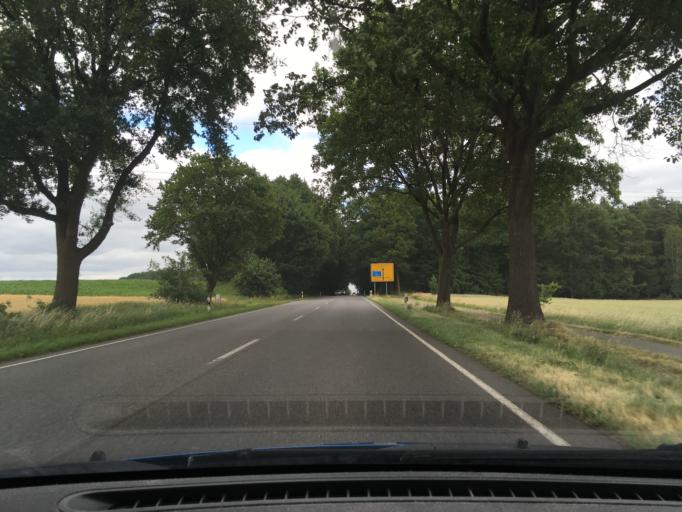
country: DE
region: Lower Saxony
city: Kakenstorf
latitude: 53.3234
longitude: 9.8028
